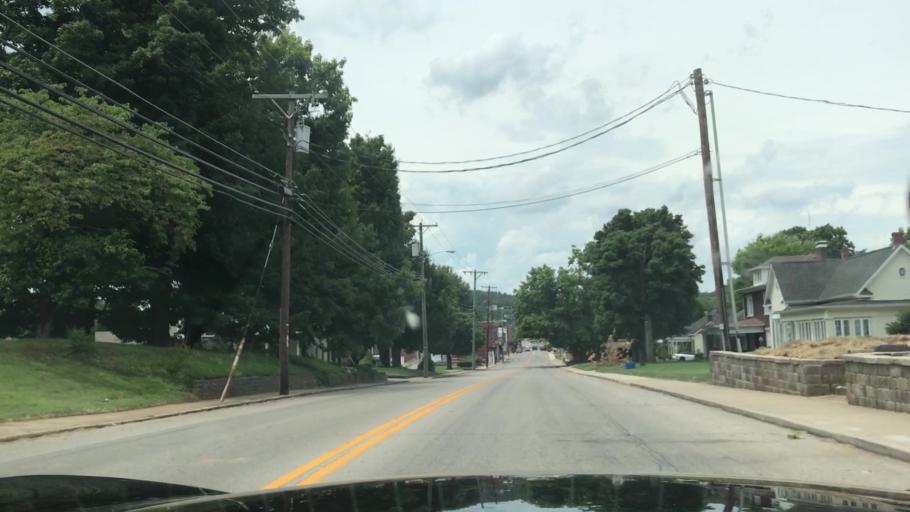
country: US
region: Kentucky
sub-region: Hart County
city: Horse Cave
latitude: 37.1790
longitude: -85.9020
